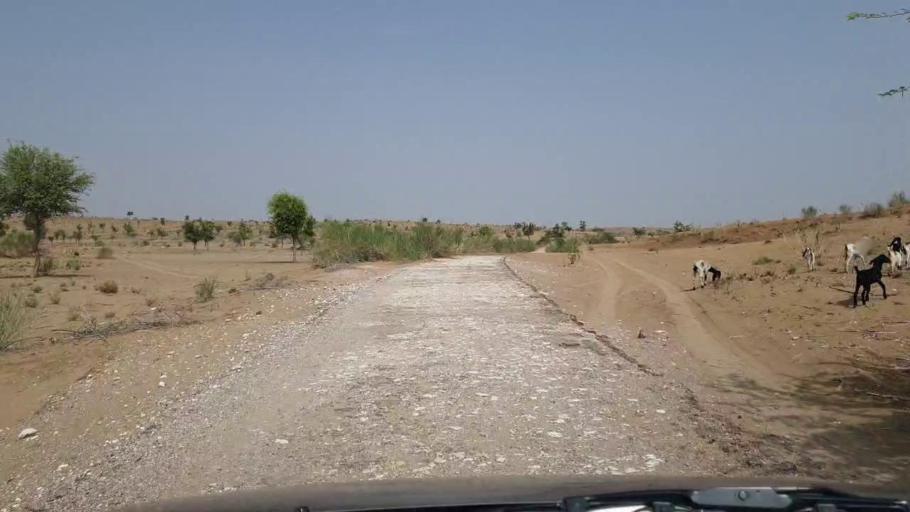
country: PK
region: Sindh
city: Chor
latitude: 25.4714
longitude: 70.5182
